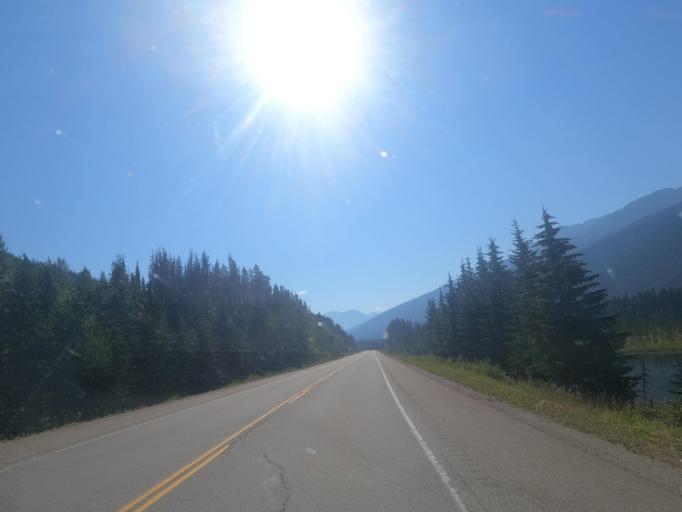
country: CA
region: Alberta
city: Jasper Park Lodge
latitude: 52.8914
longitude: -118.7299
